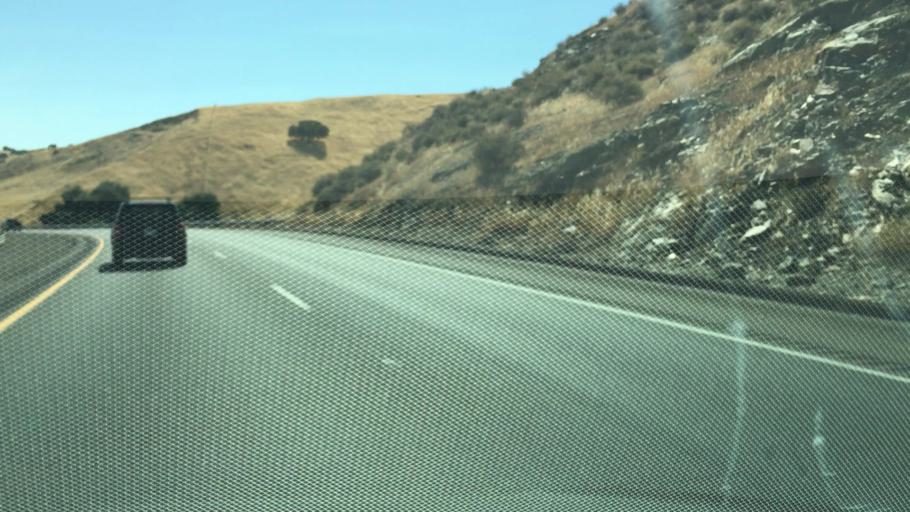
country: US
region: California
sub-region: Merced County
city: Gustine
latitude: 37.0972
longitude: -121.1513
